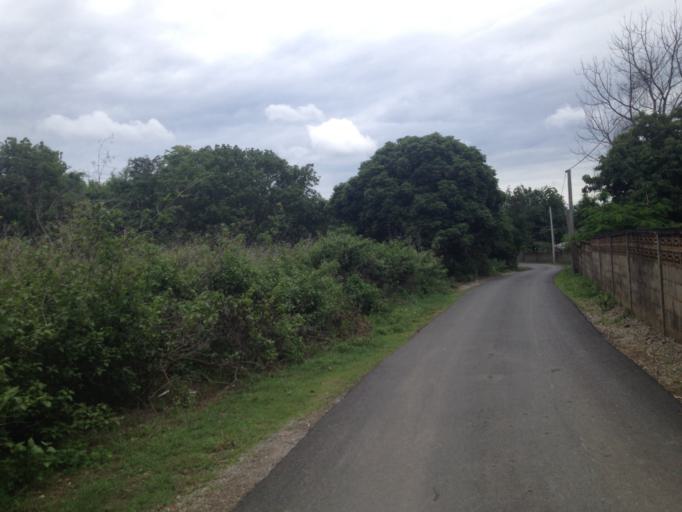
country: TH
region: Chiang Mai
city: Hang Dong
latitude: 18.7160
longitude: 98.9052
